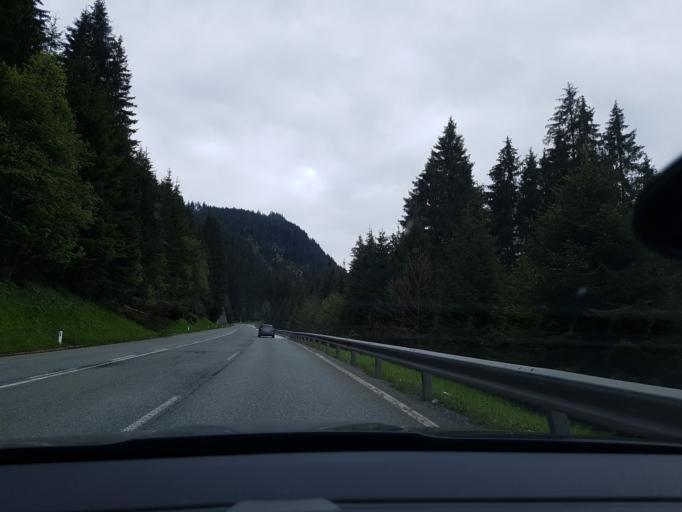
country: AT
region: Tyrol
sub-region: Politischer Bezirk Kitzbuhel
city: Jochberg
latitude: 47.3241
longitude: 12.4096
